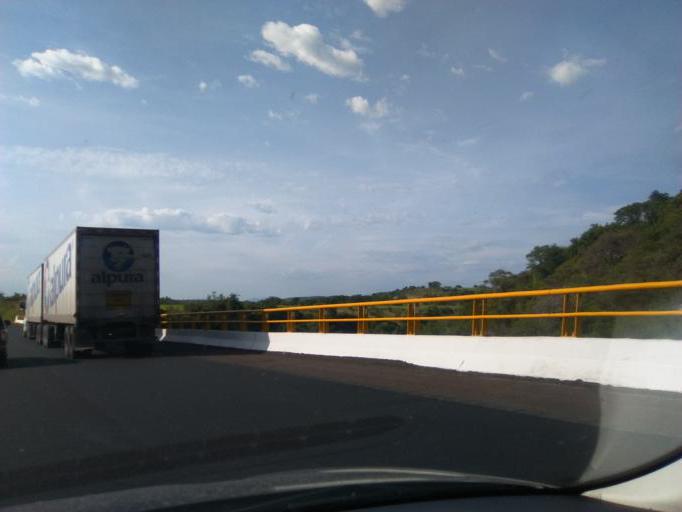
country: MX
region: Morelos
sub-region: Jojutla
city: Higueron
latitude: 18.5628
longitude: -99.2159
